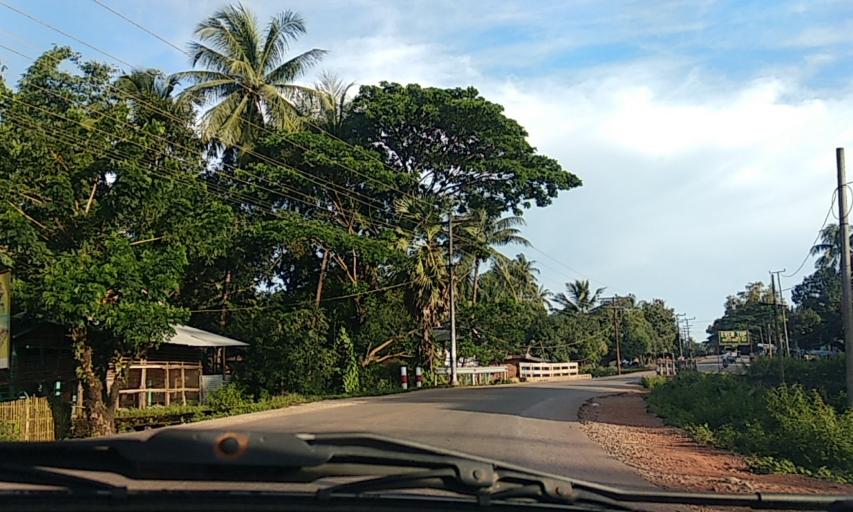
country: MM
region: Mon
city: Mawlamyine
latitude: 16.4105
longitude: 97.7004
